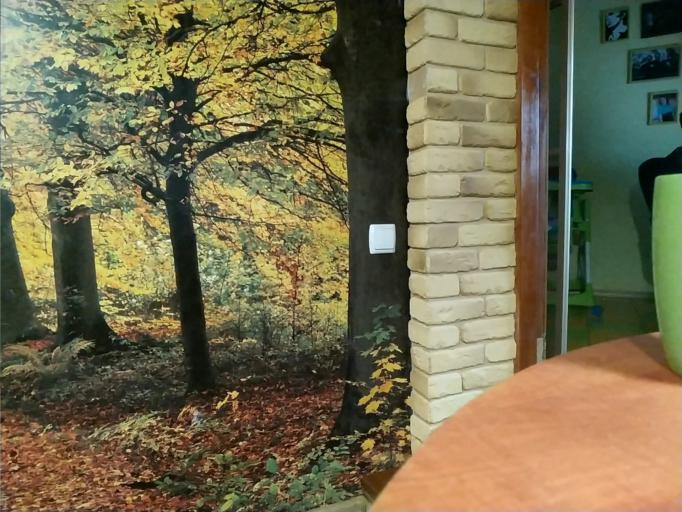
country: RU
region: Tverskaya
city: Staraya Toropa
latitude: 56.3446
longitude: 31.8372
